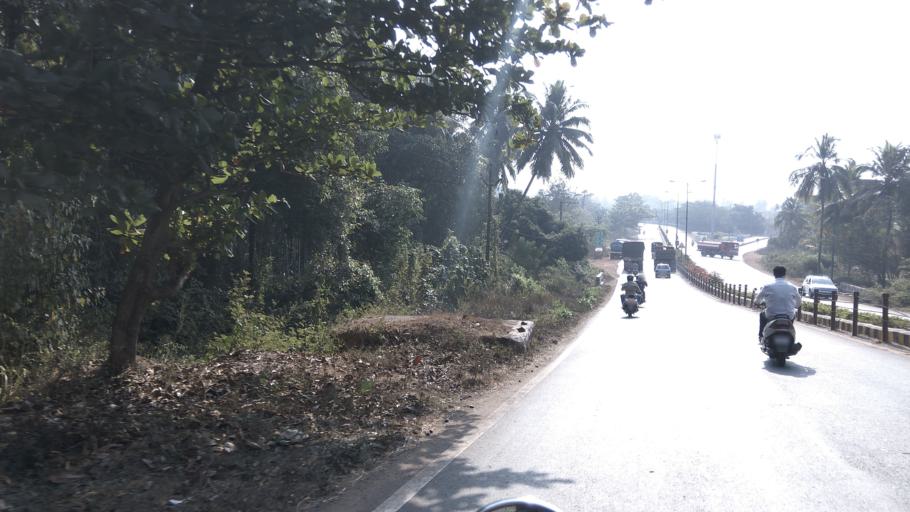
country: IN
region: Goa
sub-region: North Goa
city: Bandora
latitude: 15.4514
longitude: 73.9661
